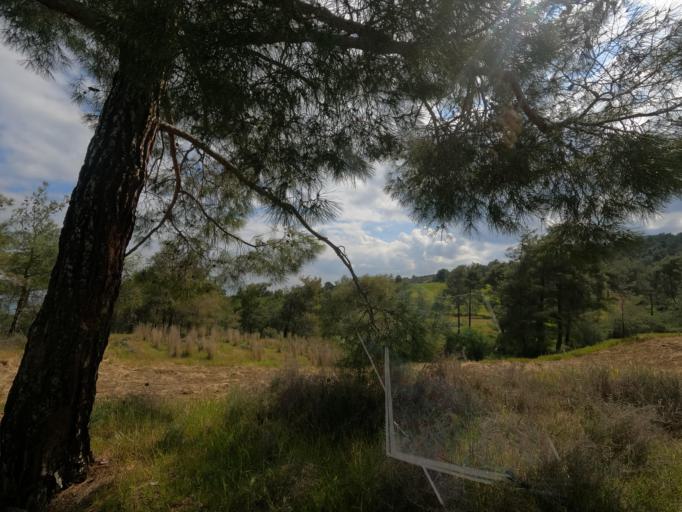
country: CY
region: Lefkosia
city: Astromeritis
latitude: 35.0730
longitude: 32.9625
